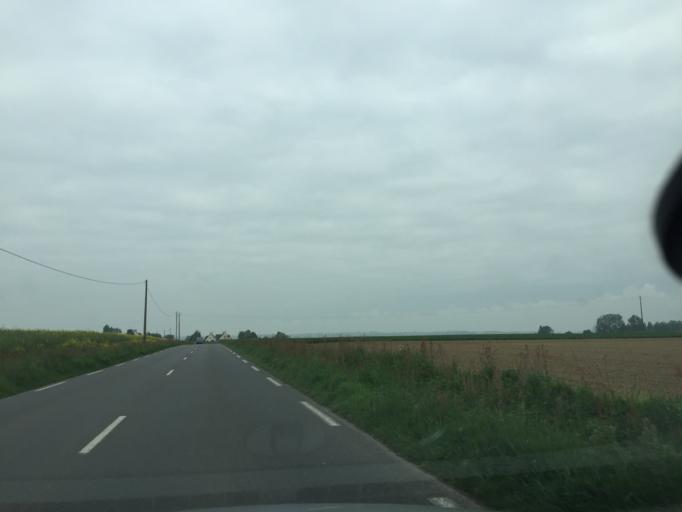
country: FR
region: Brittany
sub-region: Departement des Cotes-d'Armor
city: Matignon
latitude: 48.5898
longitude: -2.3053
